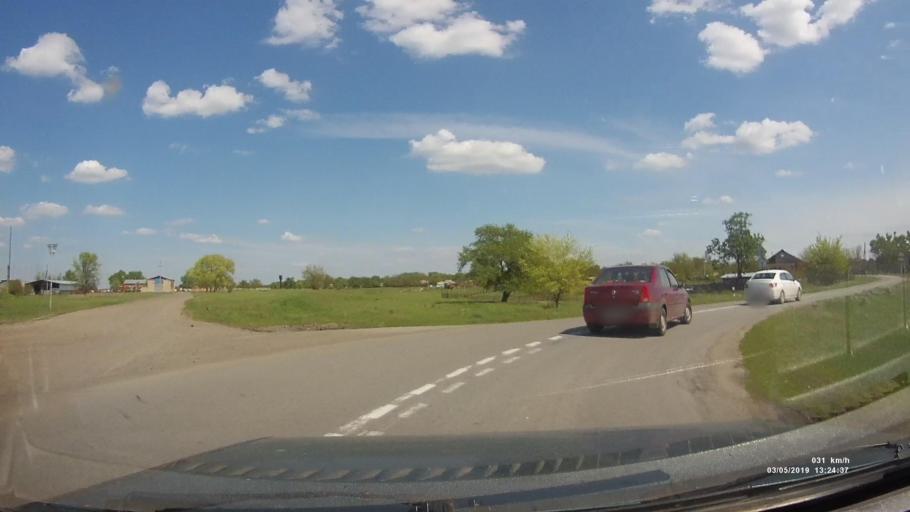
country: RU
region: Rostov
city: Semikarakorsk
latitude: 47.5659
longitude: 40.7977
